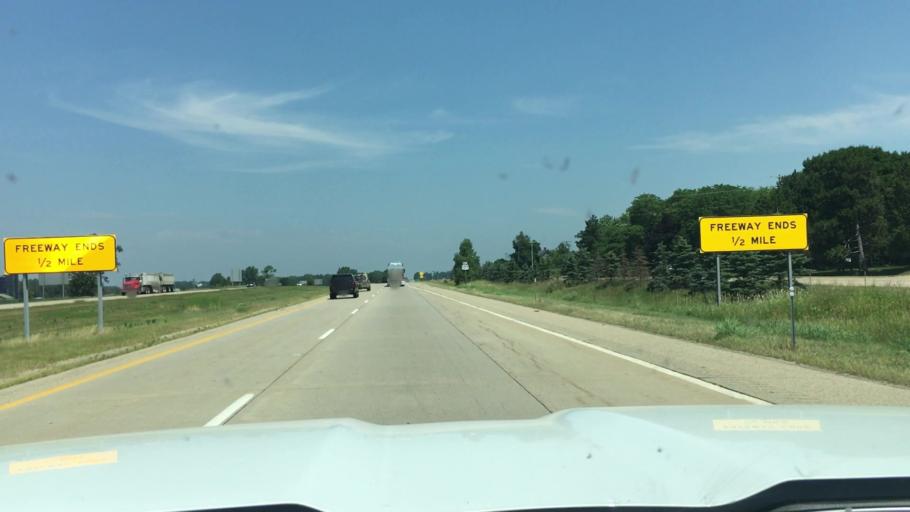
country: US
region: Michigan
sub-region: Clinton County
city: Saint Johns
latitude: 43.0362
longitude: -84.5639
